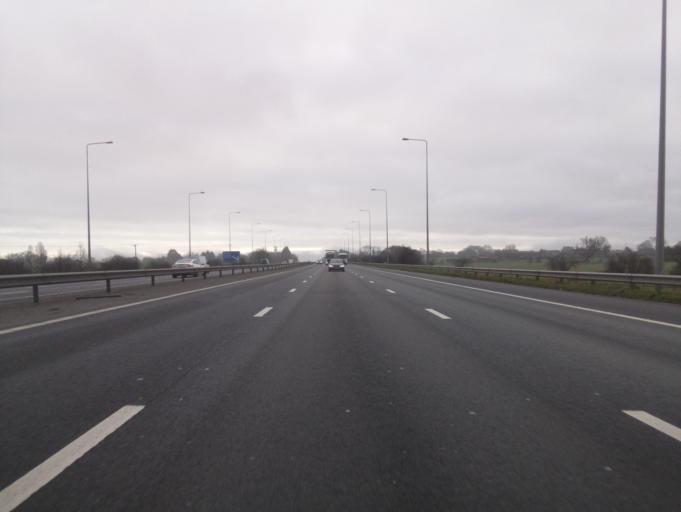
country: GB
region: England
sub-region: Borough of Wigan
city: Shevington
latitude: 53.6023
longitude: -2.6912
